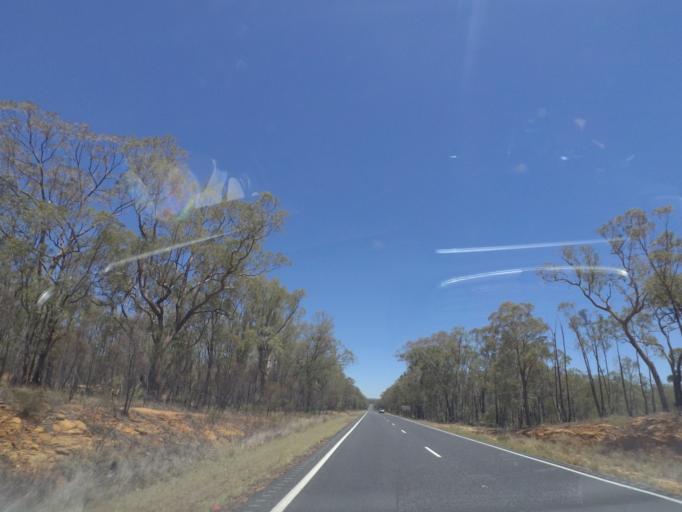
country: AU
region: New South Wales
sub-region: Warrumbungle Shire
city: Coonabarabran
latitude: -31.2146
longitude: 149.3283
